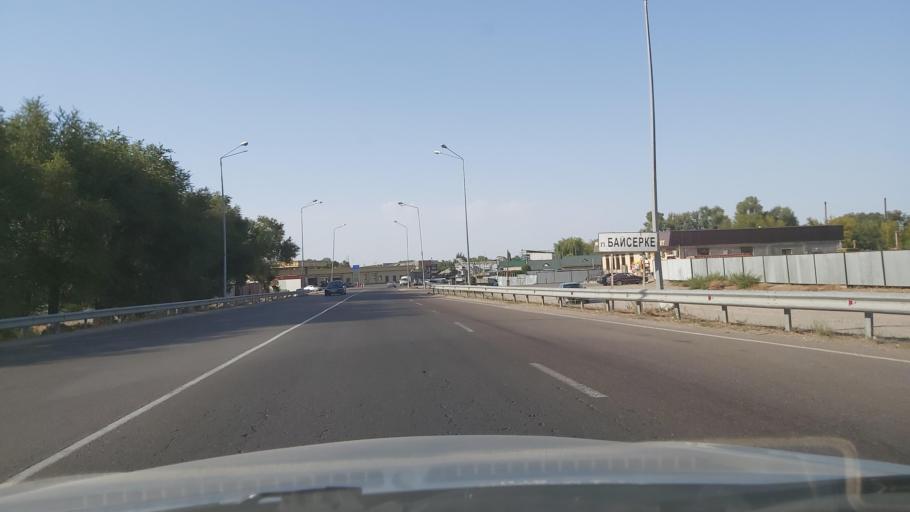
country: KZ
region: Almaty Oblysy
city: Energeticheskiy
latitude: 43.4746
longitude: 77.0313
